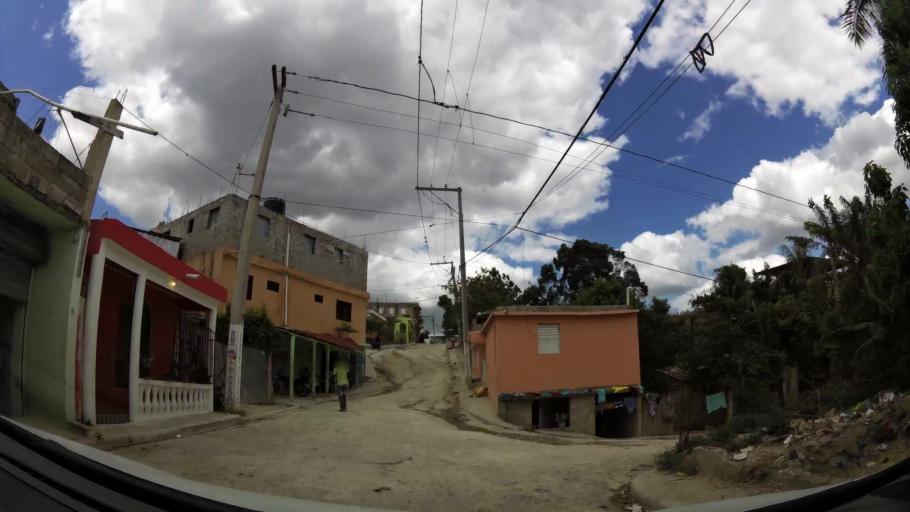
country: DO
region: Nacional
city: Ensanche Luperon
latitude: 18.5148
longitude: -69.9019
